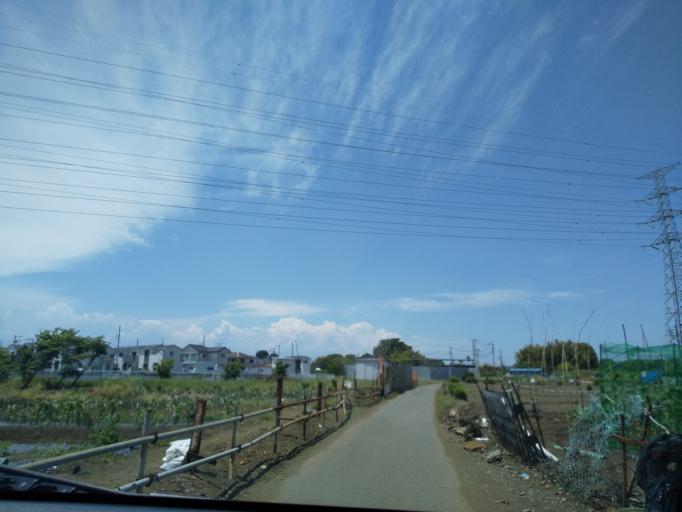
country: JP
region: Kanagawa
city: Zama
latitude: 35.5380
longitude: 139.3729
